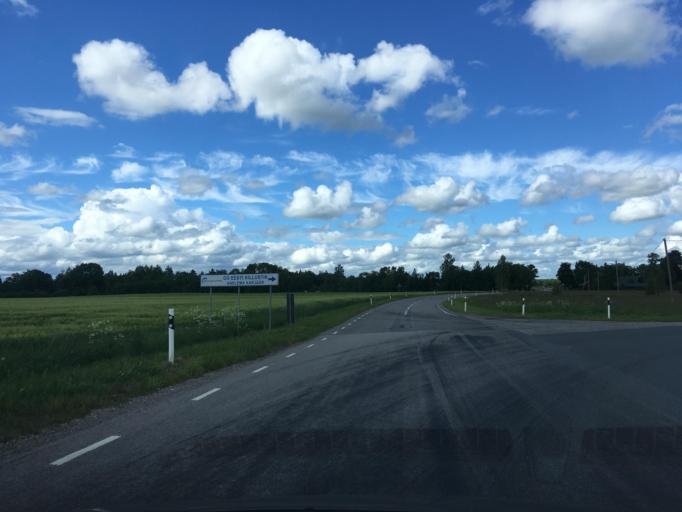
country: EE
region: Paernumaa
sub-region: Halinga vald
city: Parnu-Jaagupi
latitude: 58.6270
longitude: 24.5431
